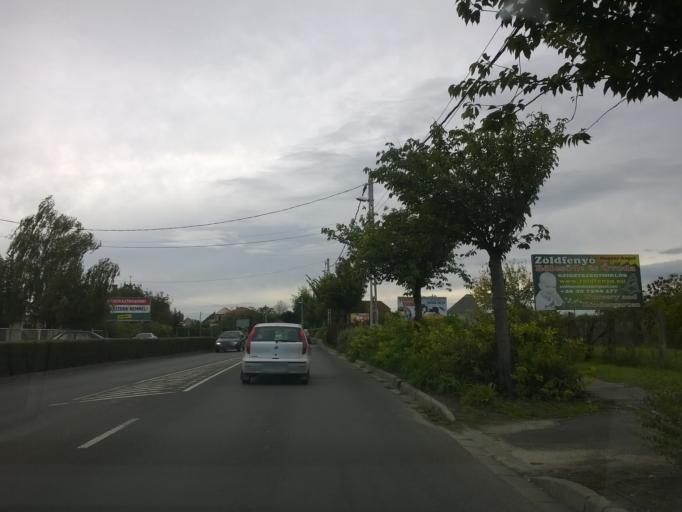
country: HU
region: Pest
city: Szigetszentmiklos
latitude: 47.3492
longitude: 19.0430
